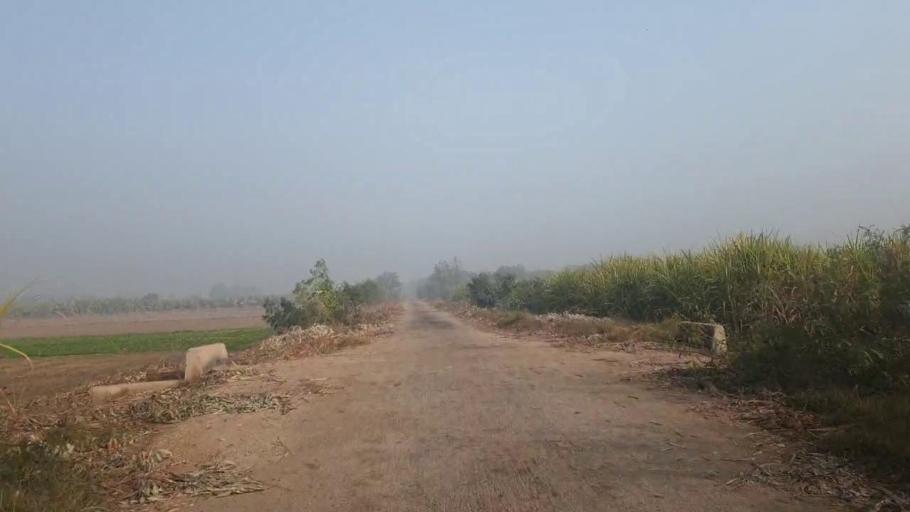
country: PK
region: Sindh
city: Tando Adam
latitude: 25.7982
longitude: 68.6334
